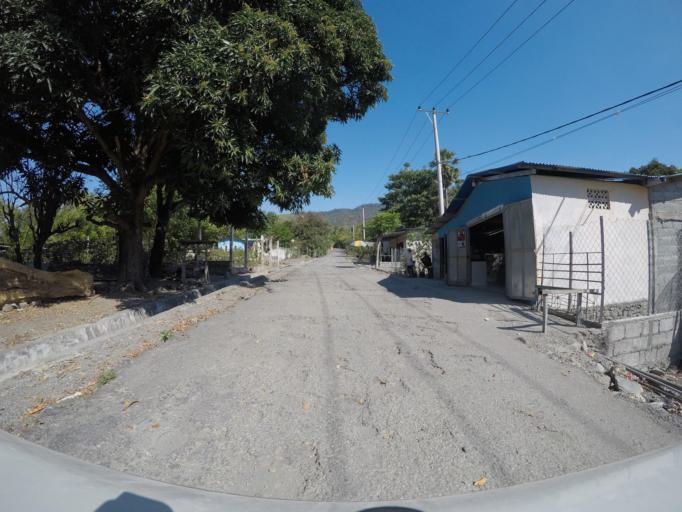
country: TL
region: Liquica
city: Maubara
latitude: -8.6143
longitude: 125.2069
